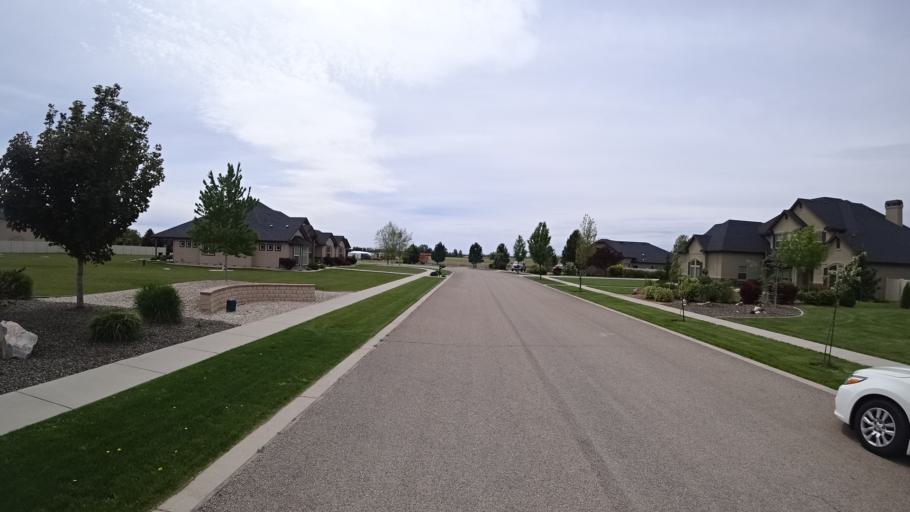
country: US
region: Idaho
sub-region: Ada County
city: Kuna
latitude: 43.5391
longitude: -116.4026
